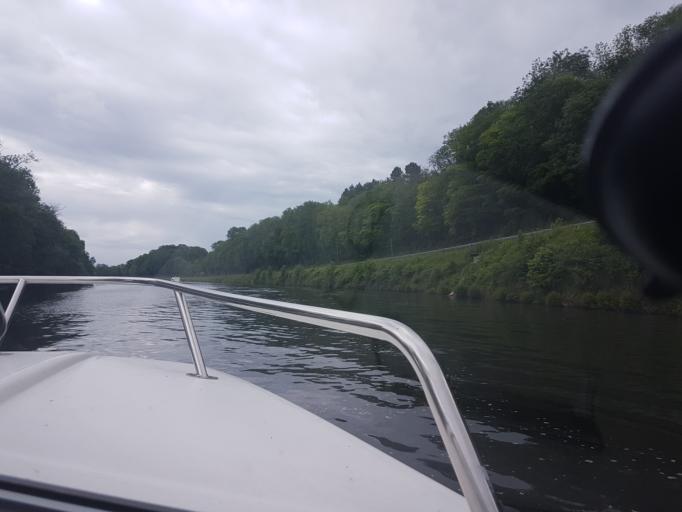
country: FR
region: Bourgogne
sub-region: Departement de l'Yonne
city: Champs-sur-Yonne
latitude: 47.7457
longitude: 3.5867
